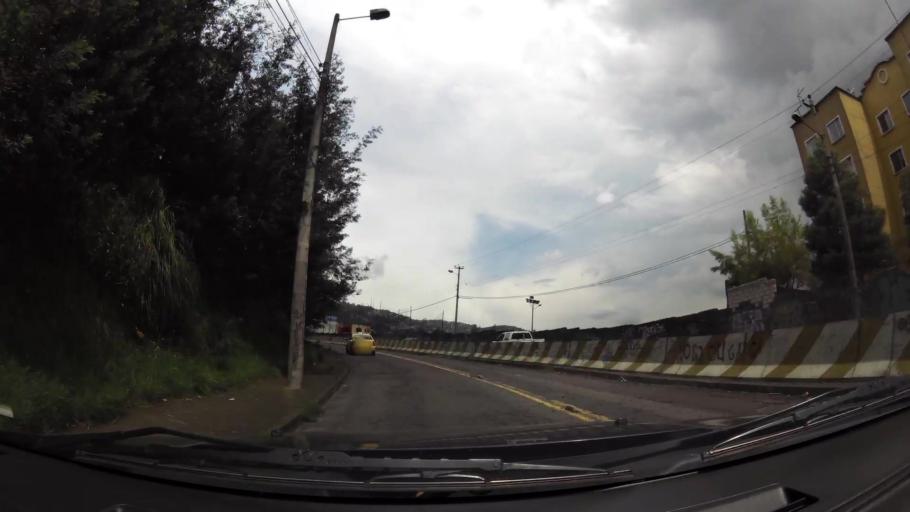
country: EC
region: Pichincha
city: Quito
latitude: -0.2360
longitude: -78.5107
